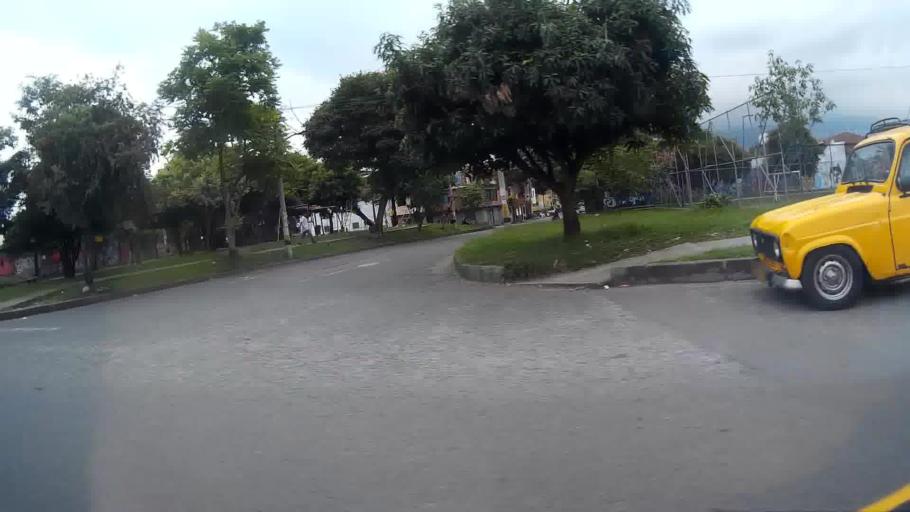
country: CO
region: Antioquia
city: Medellin
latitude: 6.2288
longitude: -75.5872
